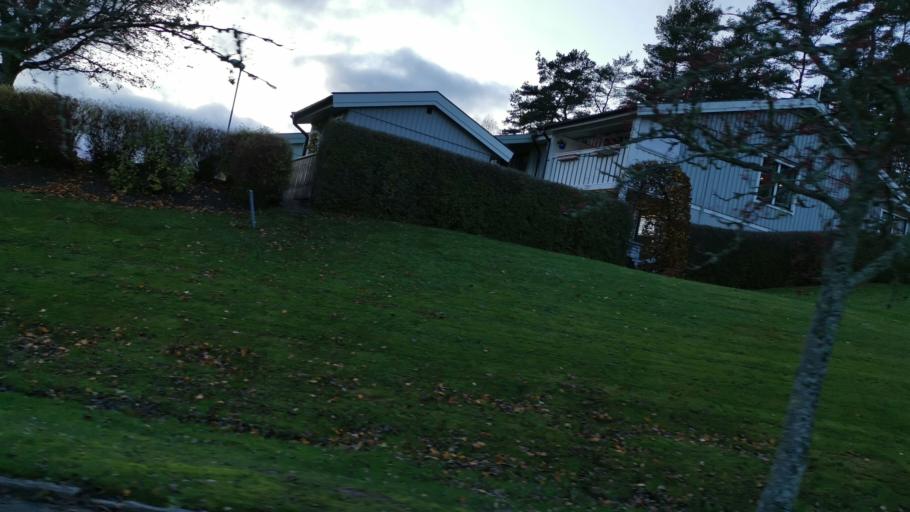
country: SE
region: Vaestra Goetaland
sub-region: Munkedals Kommun
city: Munkedal
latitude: 58.4753
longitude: 11.6709
